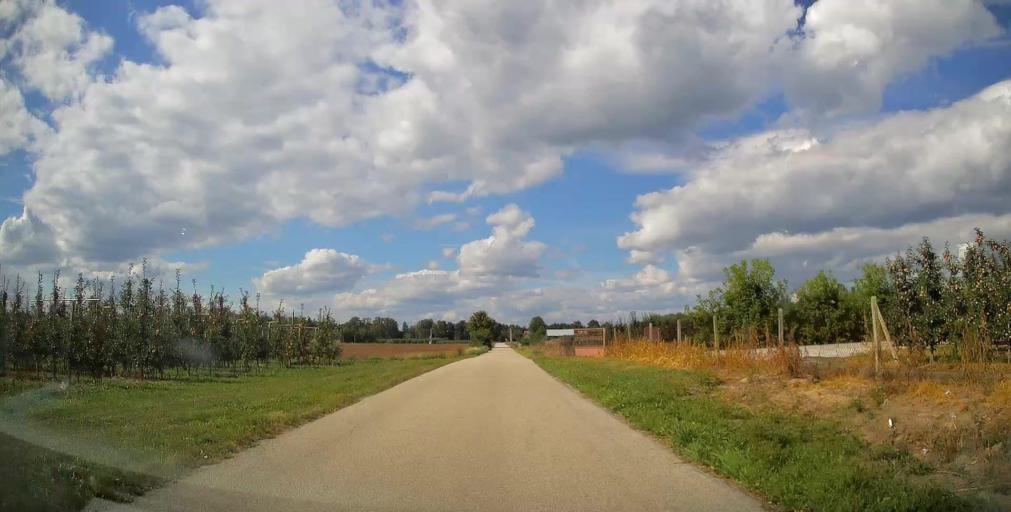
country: PL
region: Masovian Voivodeship
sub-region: Powiat grojecki
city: Goszczyn
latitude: 51.7088
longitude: 20.8911
